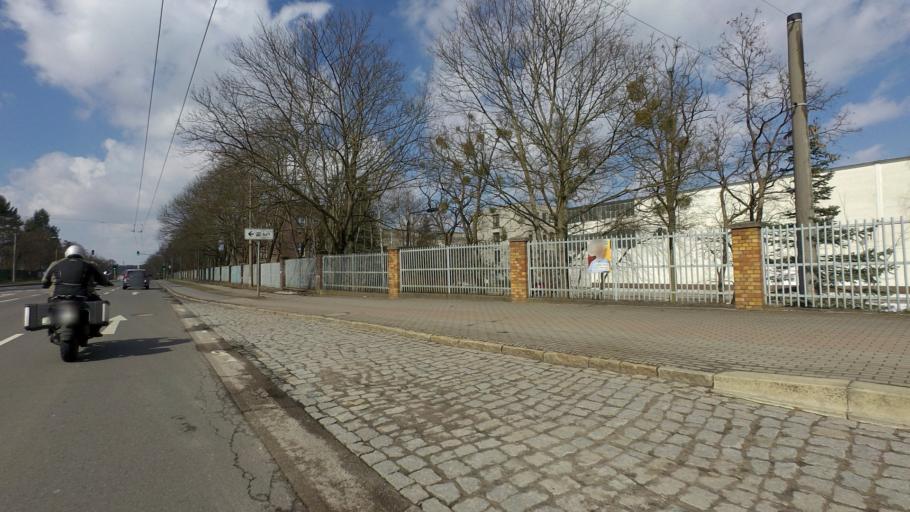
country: DE
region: Brandenburg
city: Eberswalde
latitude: 52.8387
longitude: 13.7790
